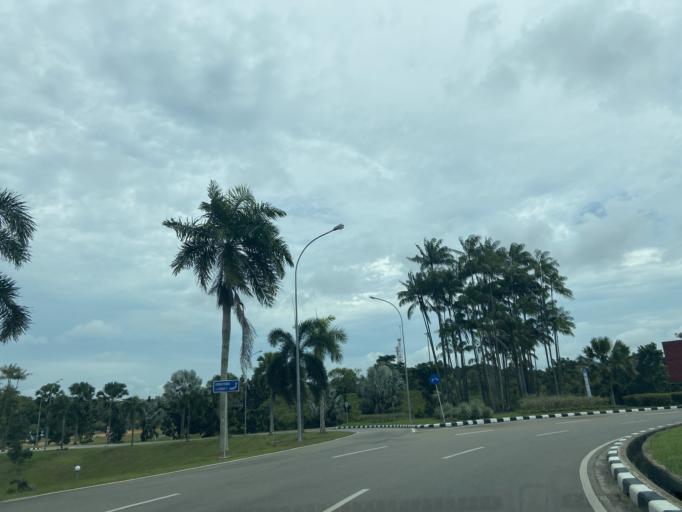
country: SG
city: Singapore
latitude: 1.1230
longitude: 104.1126
